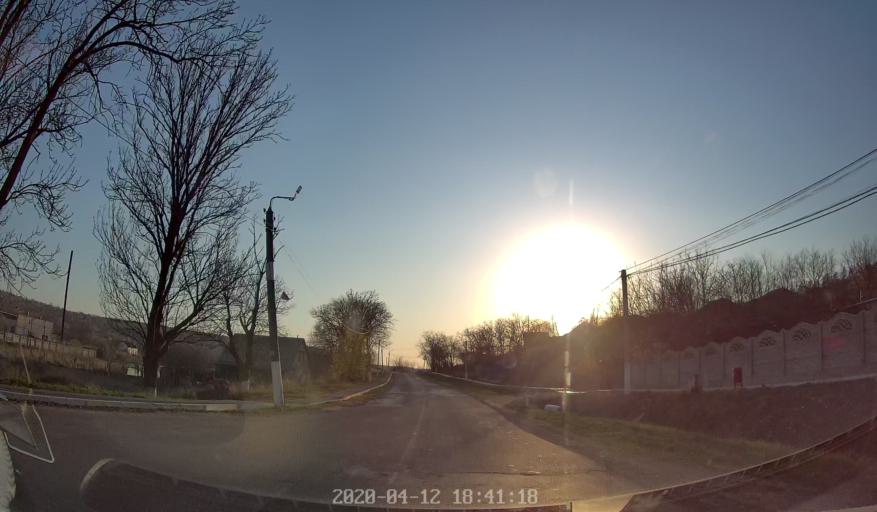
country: MD
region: Chisinau
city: Ciorescu
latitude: 47.1357
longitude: 28.9539
